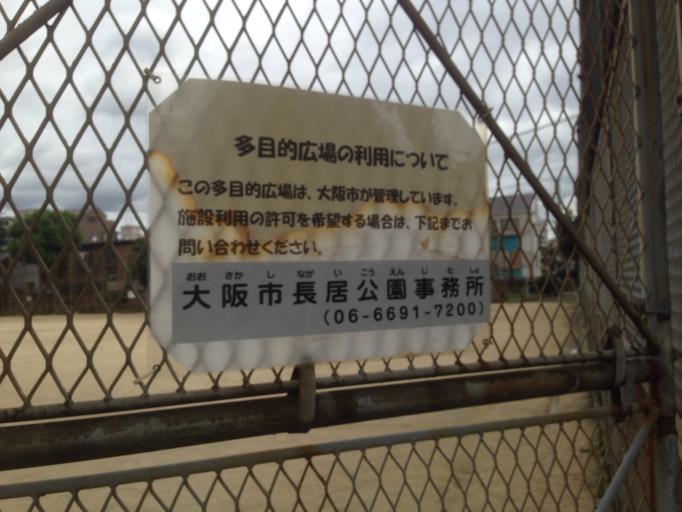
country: JP
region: Osaka
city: Sakai
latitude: 34.5989
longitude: 135.5071
